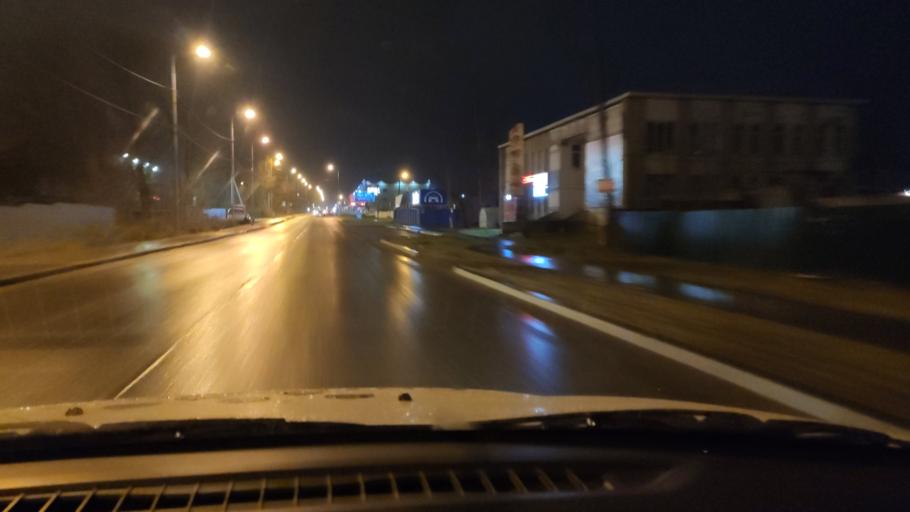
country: RU
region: Perm
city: Kondratovo
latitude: 57.9631
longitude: 56.1575
